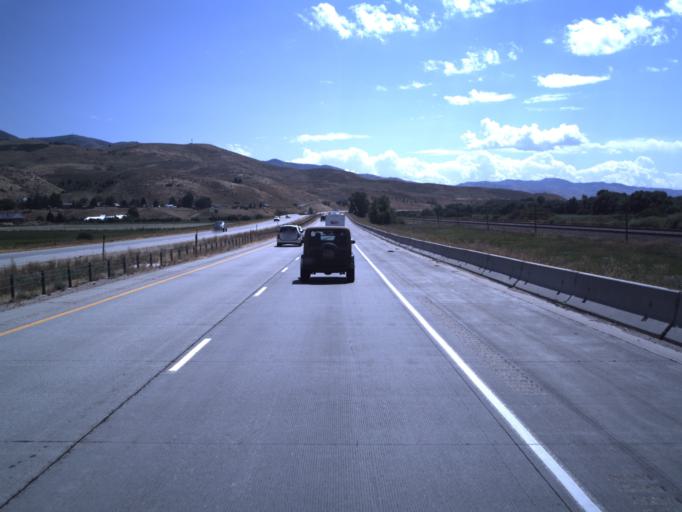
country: US
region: Utah
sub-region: Morgan County
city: Mountain Green
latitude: 41.1343
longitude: -111.7834
